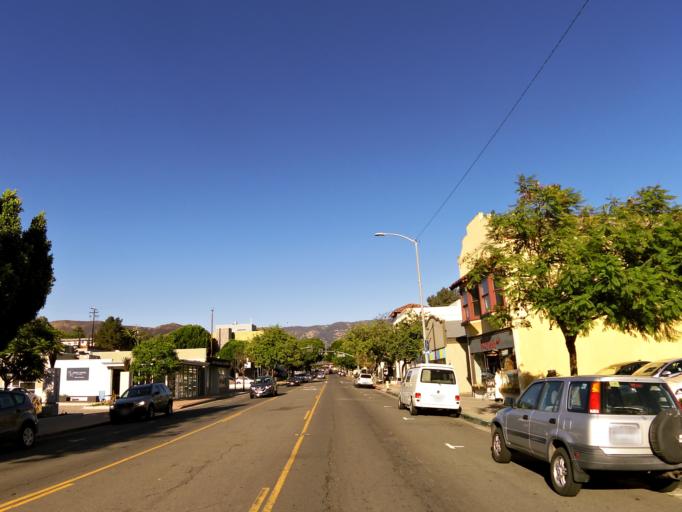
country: US
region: California
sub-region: San Luis Obispo County
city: San Luis Obispo
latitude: 35.2836
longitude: -120.6582
